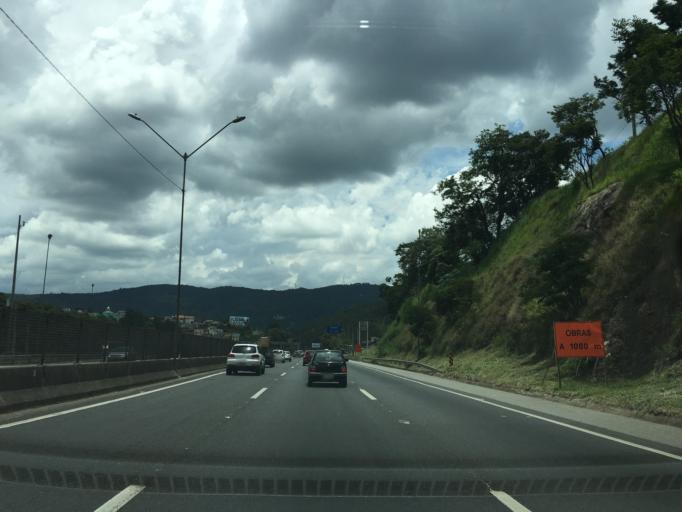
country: BR
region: Sao Paulo
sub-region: Mairipora
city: Mairipora
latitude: -23.3334
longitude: -46.5762
